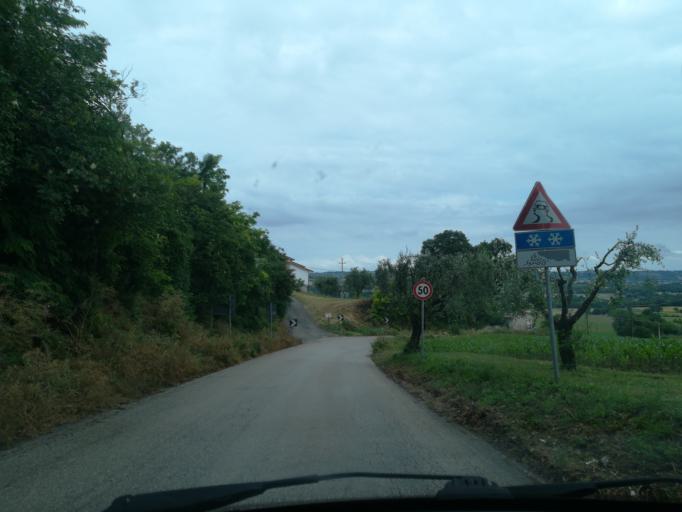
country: IT
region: The Marches
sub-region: Provincia di Macerata
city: Petriolo
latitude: 43.2259
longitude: 13.4641
